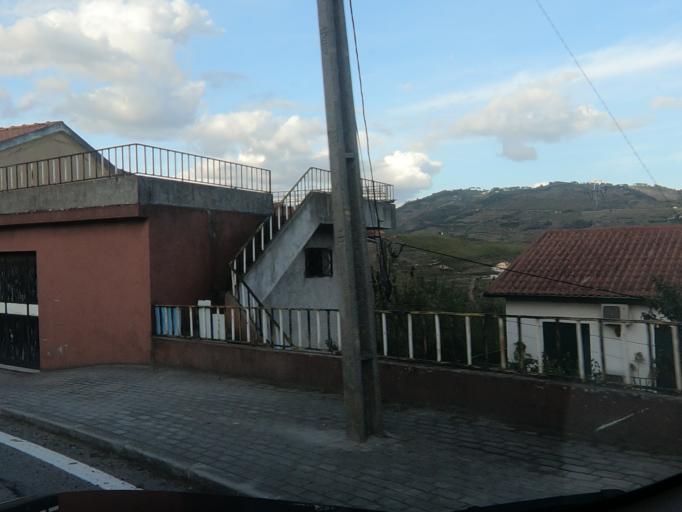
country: PT
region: Vila Real
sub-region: Santa Marta de Penaguiao
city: Santa Marta de Penaguiao
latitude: 41.1967
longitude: -7.7771
